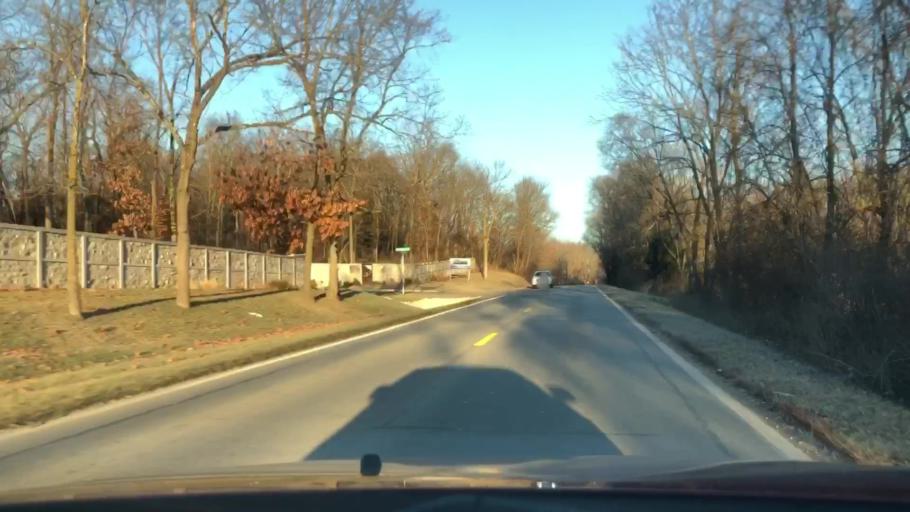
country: US
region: Missouri
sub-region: Greene County
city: Springfield
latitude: 37.1604
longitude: -93.2425
